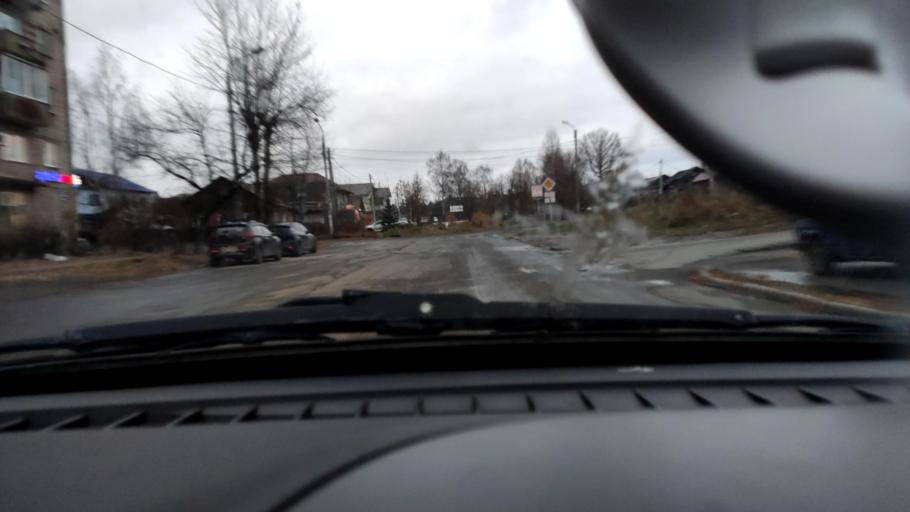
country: RU
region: Perm
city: Kondratovo
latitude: 58.0483
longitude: 56.0940
